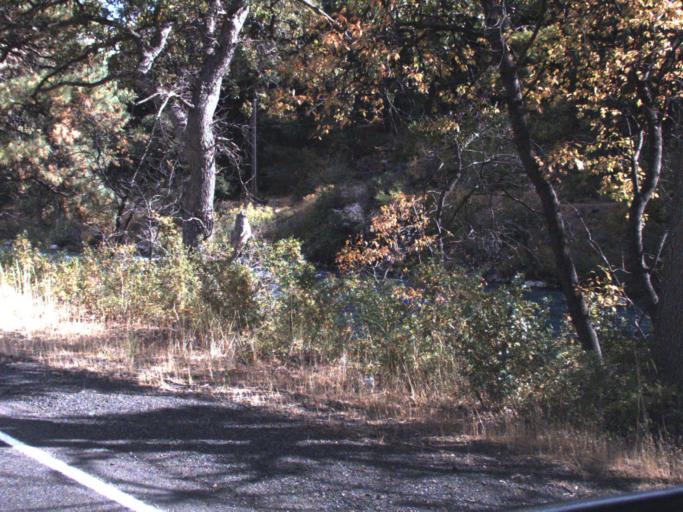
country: US
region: Washington
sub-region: Yakima County
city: Tieton
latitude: 46.6821
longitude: -120.9563
